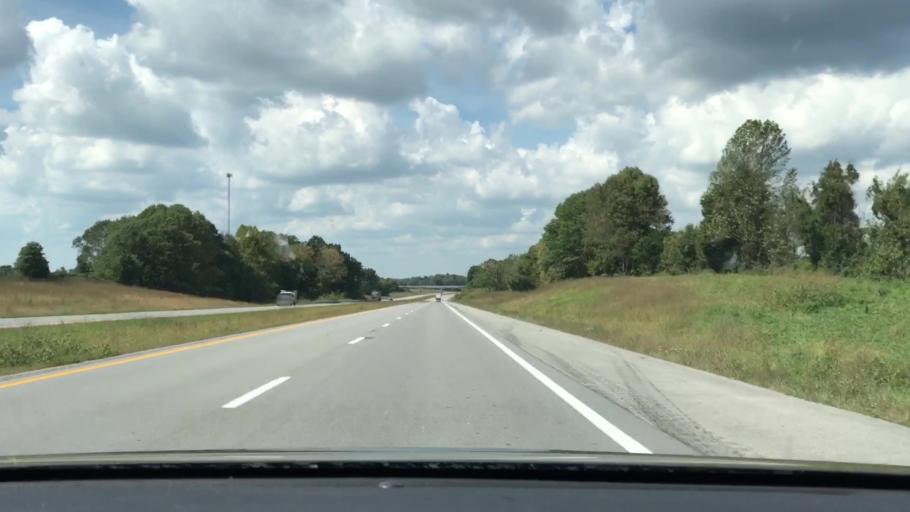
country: US
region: Kentucky
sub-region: Russell County
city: Russell Springs
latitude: 37.0512
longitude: -85.1563
